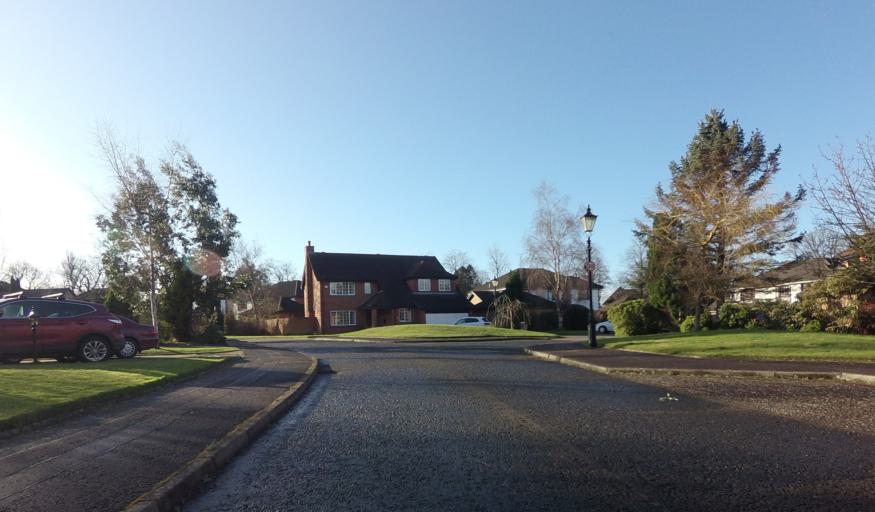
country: GB
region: Scotland
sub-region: Edinburgh
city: Currie
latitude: 55.9697
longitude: -3.3037
